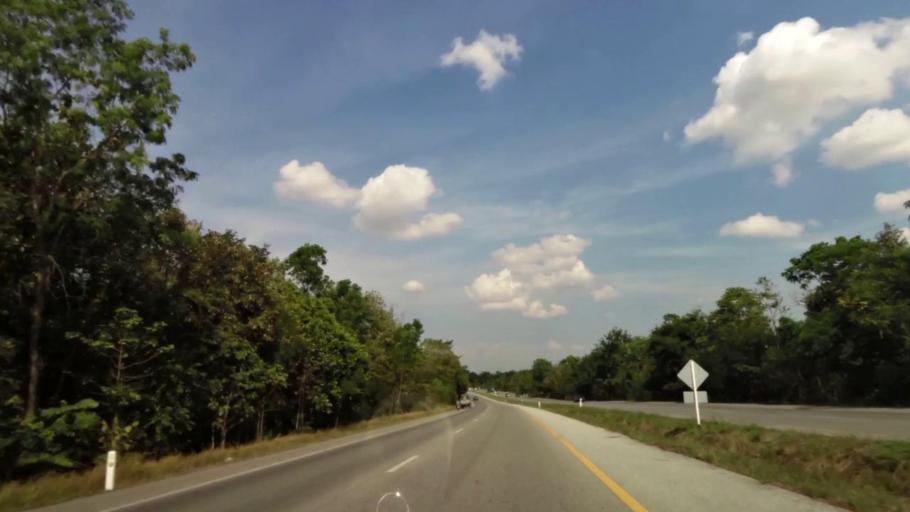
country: TH
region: Uttaradit
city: Thong Saen Khan
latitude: 17.4567
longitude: 100.2378
